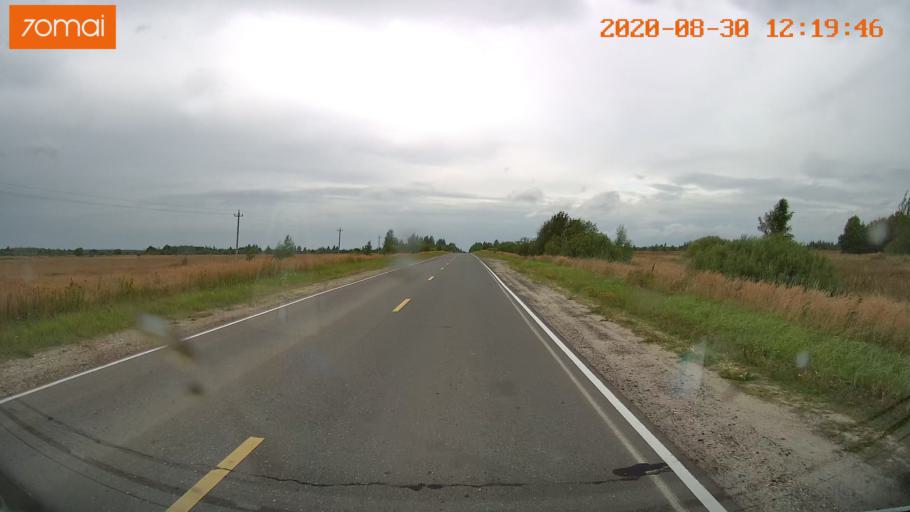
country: RU
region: Ivanovo
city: Yur'yevets
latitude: 57.3230
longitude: 42.9187
